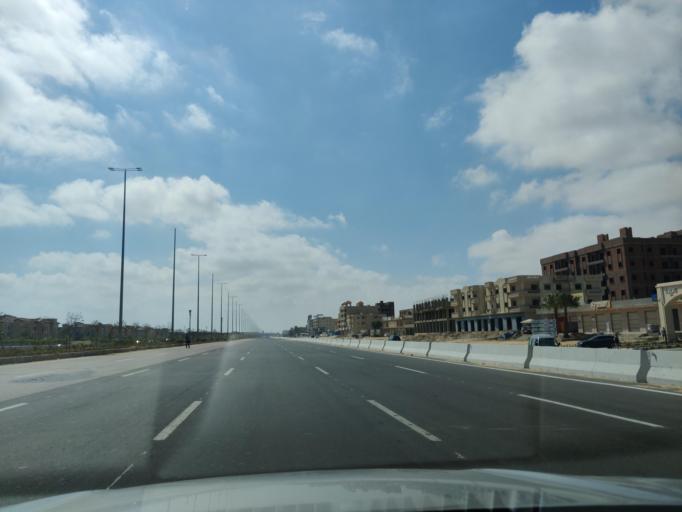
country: EG
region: Muhafazat Matruh
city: Al `Alamayn
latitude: 30.9656
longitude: 28.7488
